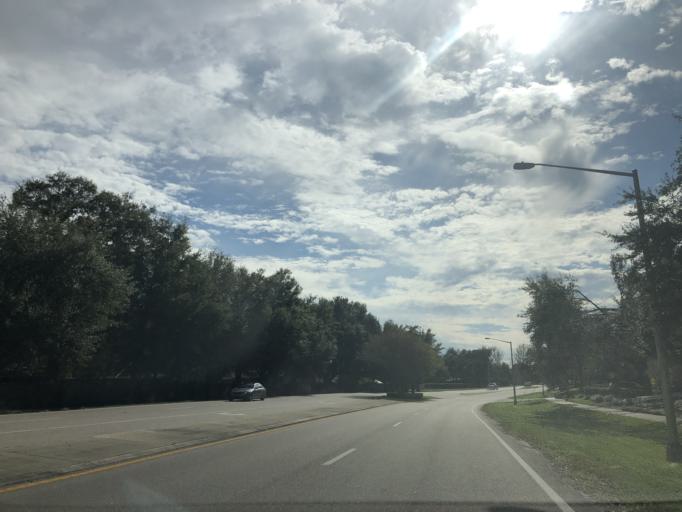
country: US
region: Florida
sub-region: Orange County
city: Bay Hill
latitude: 28.4917
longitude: -81.4909
